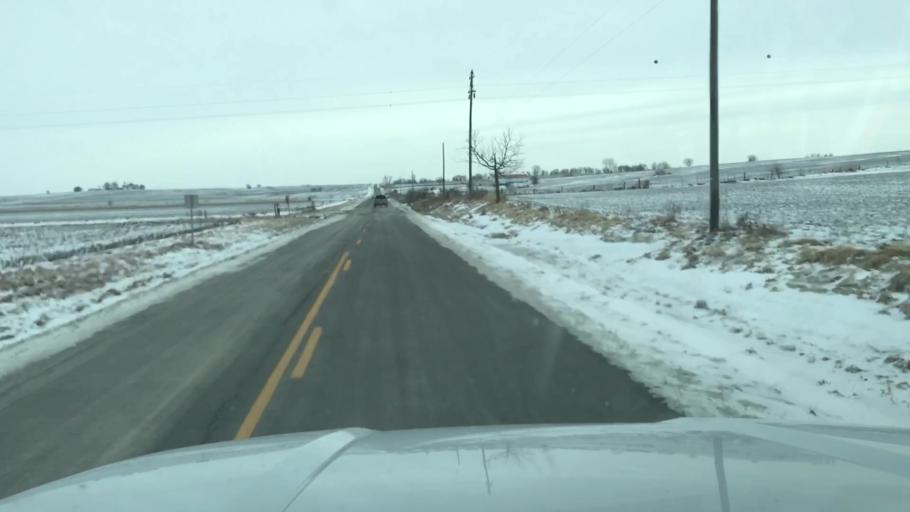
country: US
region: Missouri
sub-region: Holt County
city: Oregon
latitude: 40.1289
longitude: -95.0224
